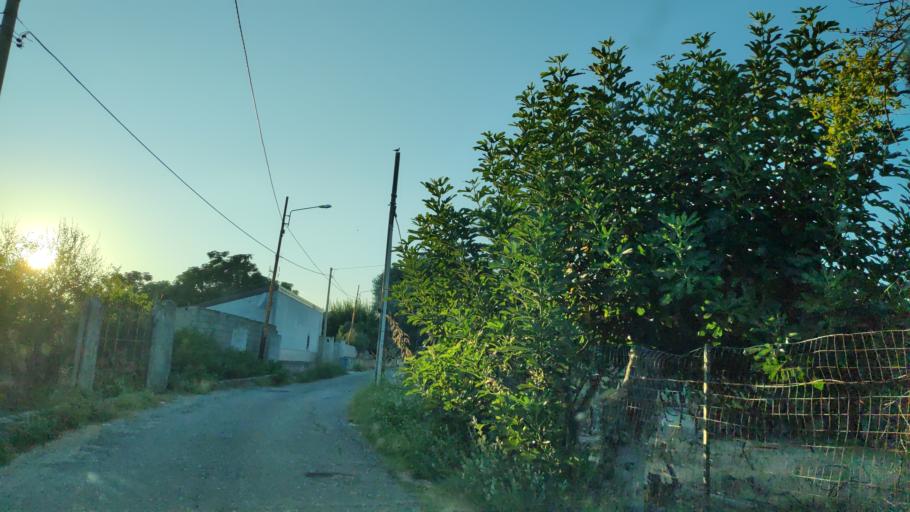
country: IT
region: Calabria
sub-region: Provincia di Reggio Calabria
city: Monasterace Marina
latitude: 38.4317
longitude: 16.5684
